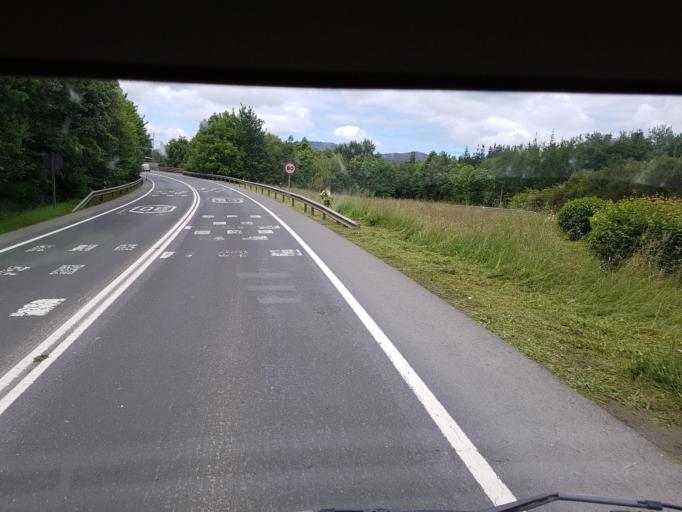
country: ES
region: Basque Country
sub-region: Bizkaia
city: Amorebieta
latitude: 43.2281
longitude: -2.7446
